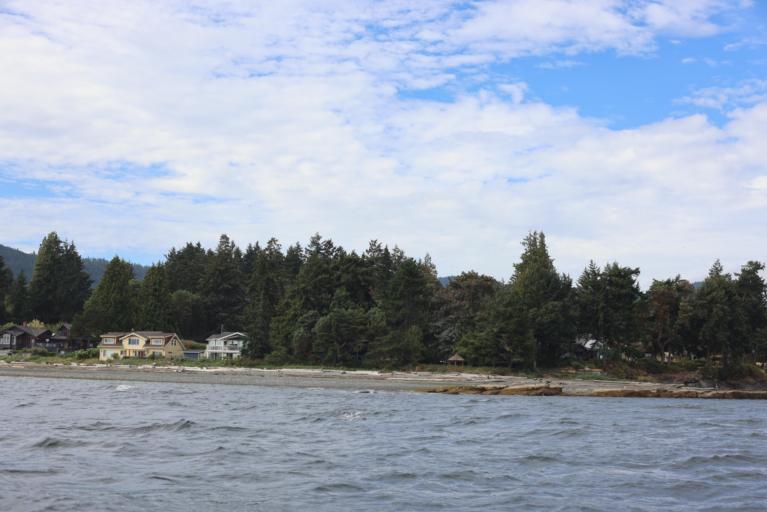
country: CA
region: British Columbia
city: Nanaimo
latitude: 49.2585
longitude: -124.0803
